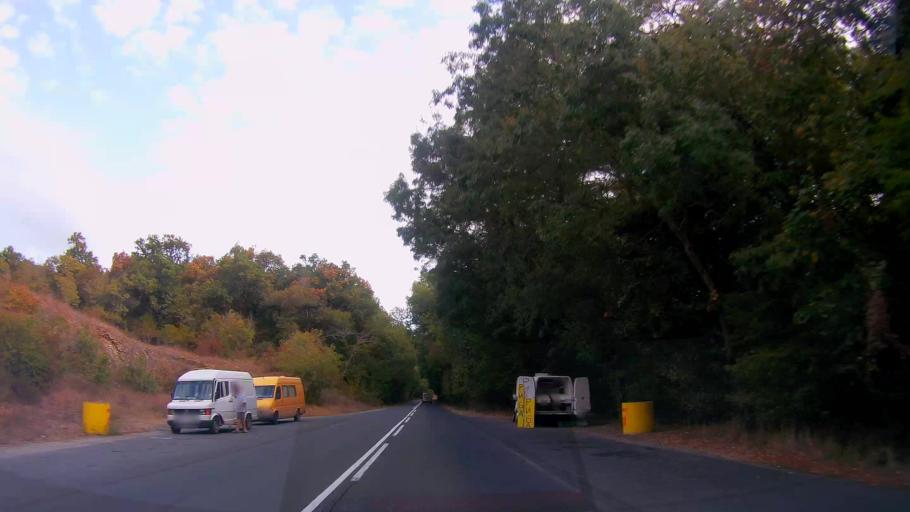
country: BG
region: Burgas
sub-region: Obshtina Primorsko
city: Primorsko
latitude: 42.3080
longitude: 27.7237
